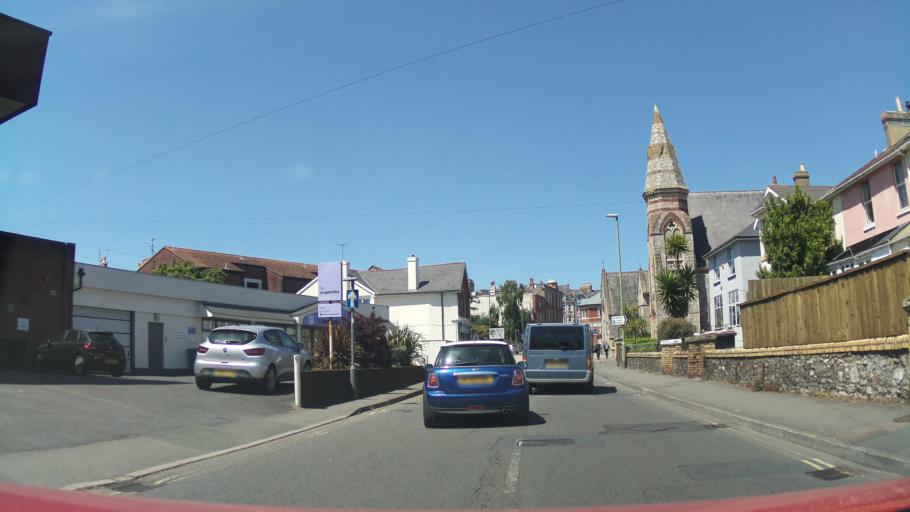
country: GB
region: England
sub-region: Borough of Torbay
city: Paignton
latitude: 50.4339
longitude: -3.5671
